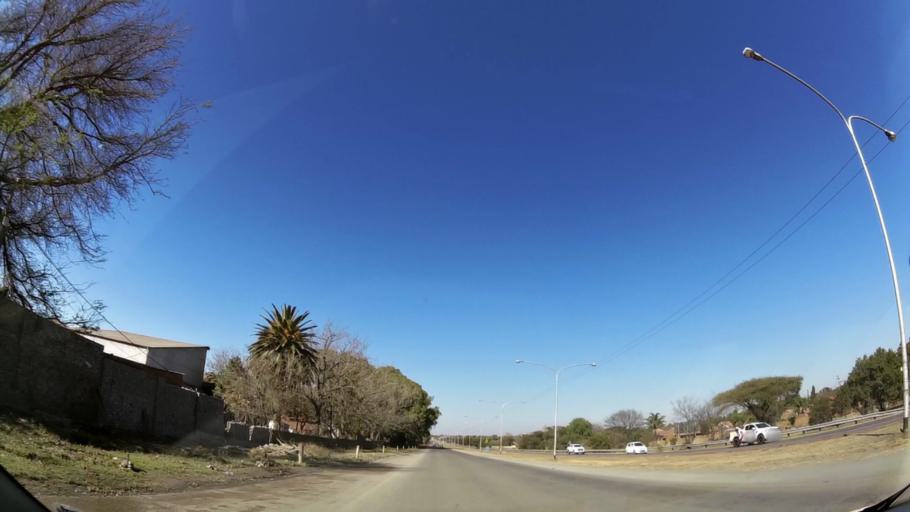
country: ZA
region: Gauteng
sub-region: City of Tshwane Metropolitan Municipality
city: Centurion
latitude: -25.8435
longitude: 28.2141
